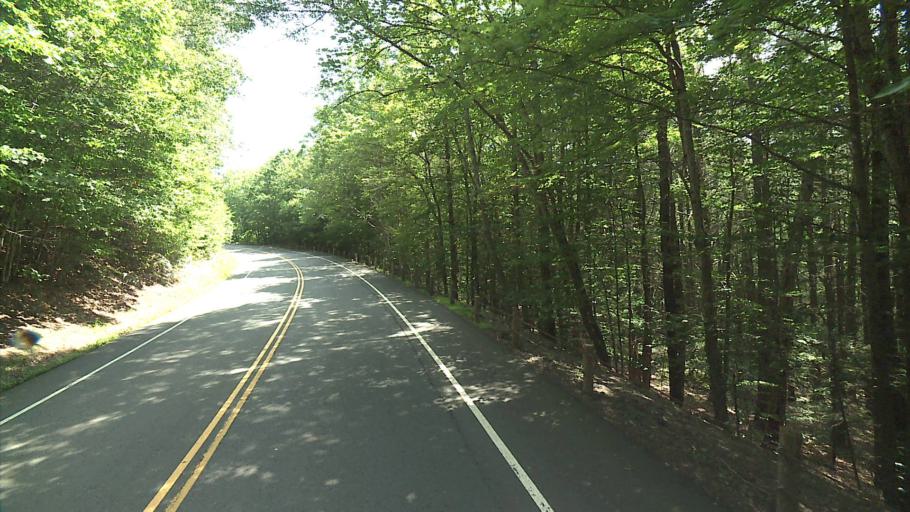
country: US
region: Massachusetts
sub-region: Hampden County
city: Granville
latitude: 42.0162
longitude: -72.9269
